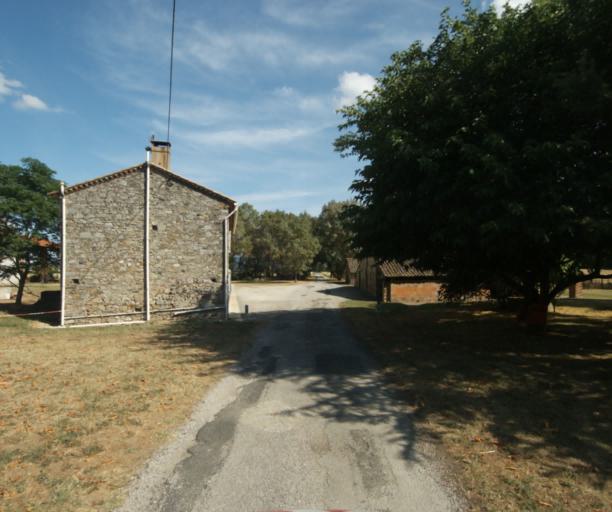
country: FR
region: Midi-Pyrenees
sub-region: Departement de la Haute-Garonne
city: Revel
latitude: 43.5116
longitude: 1.9793
